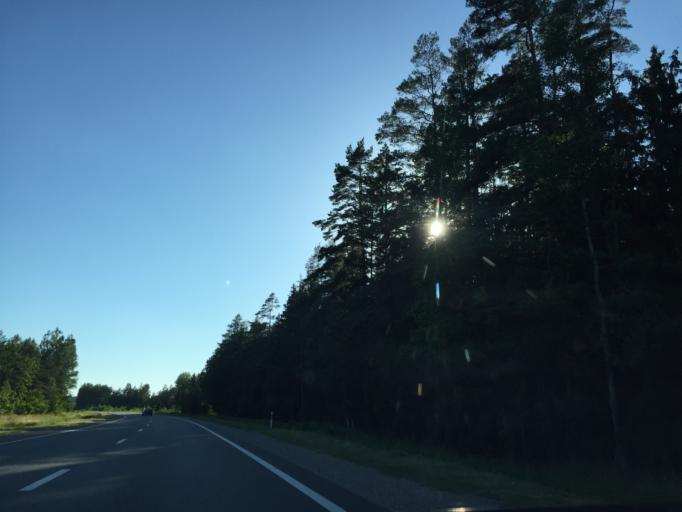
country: LV
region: Ventspils Rajons
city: Piltene
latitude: 57.3889
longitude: 21.7926
